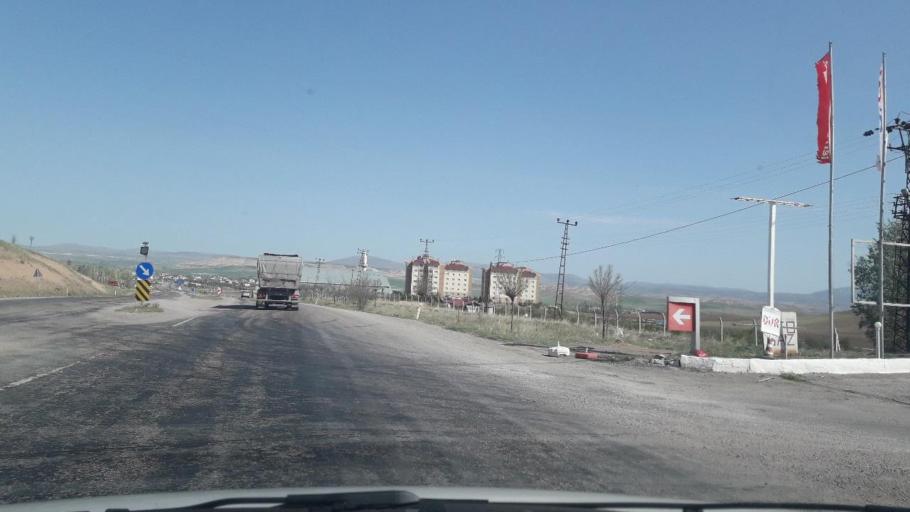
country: TR
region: Sivas
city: Kangal
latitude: 39.2202
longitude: 37.4060
